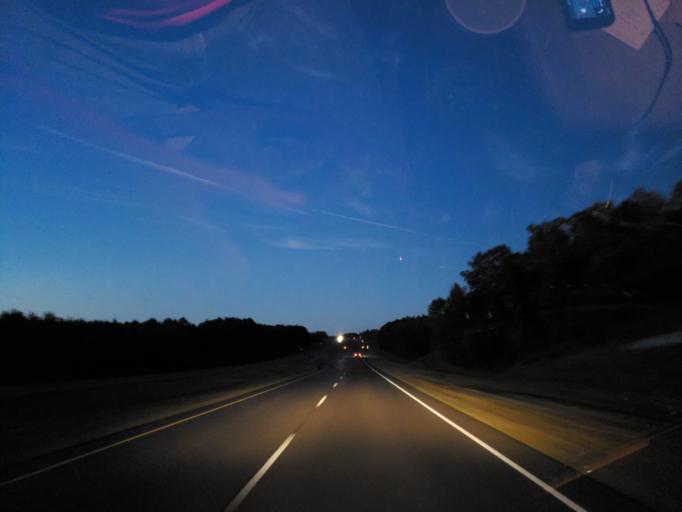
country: US
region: Mississippi
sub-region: Clarke County
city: Quitman
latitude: 32.0320
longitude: -88.6812
